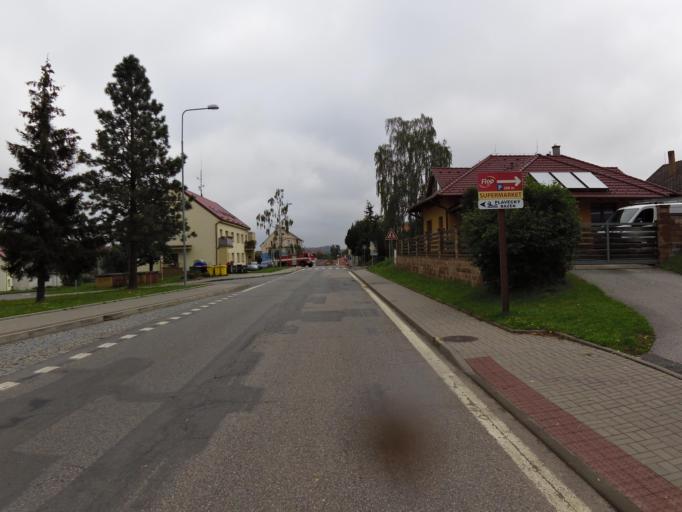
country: CZ
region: Jihocesky
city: Mlada Vozice
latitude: 49.5282
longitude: 14.8060
